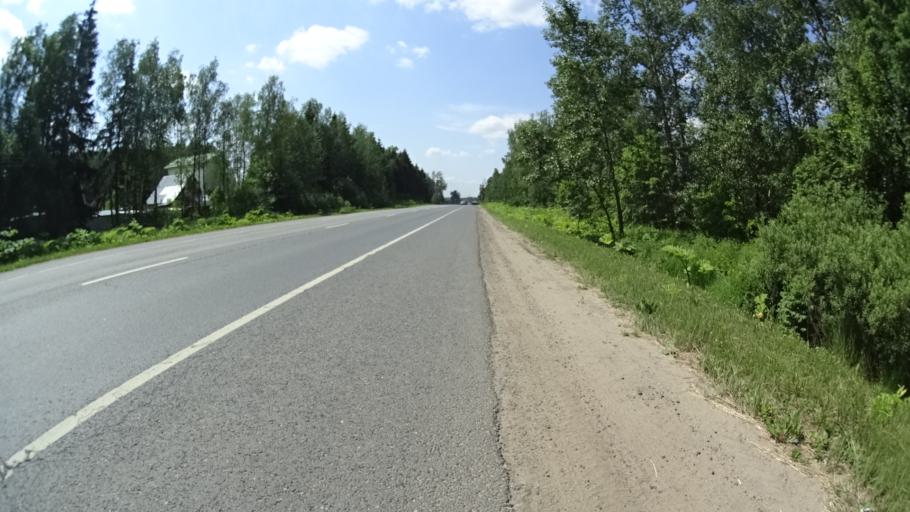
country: RU
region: Moskovskaya
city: Lesnoy
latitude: 56.0596
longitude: 38.0083
